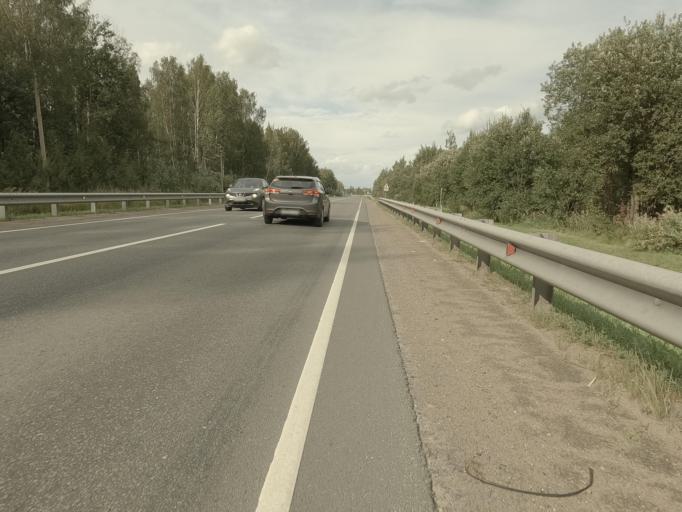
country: RU
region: Leningrad
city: Mga
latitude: 59.7882
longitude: 31.1073
